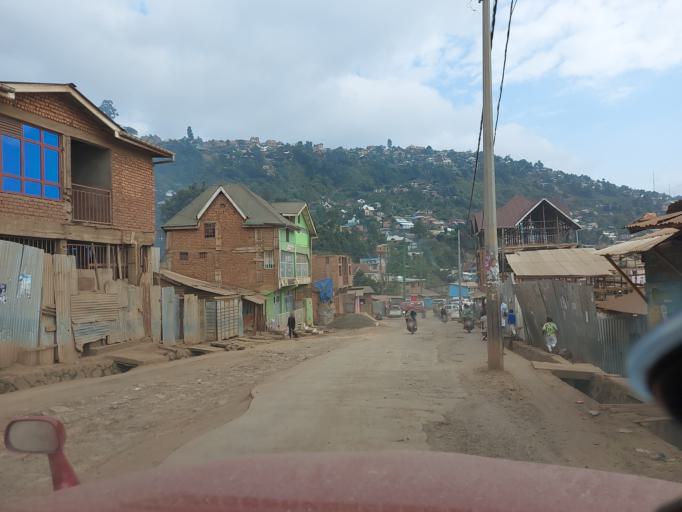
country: CD
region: South Kivu
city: Bukavu
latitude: -2.5154
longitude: 28.8497
